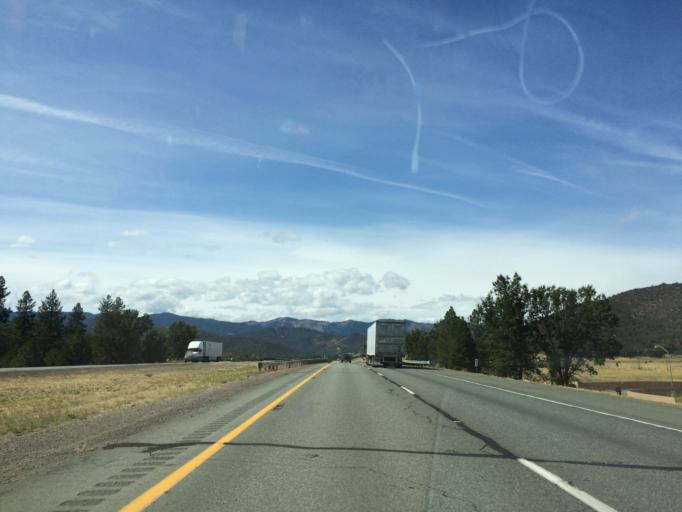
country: US
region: California
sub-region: Siskiyou County
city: Yreka
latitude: 41.6671
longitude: -122.6090
